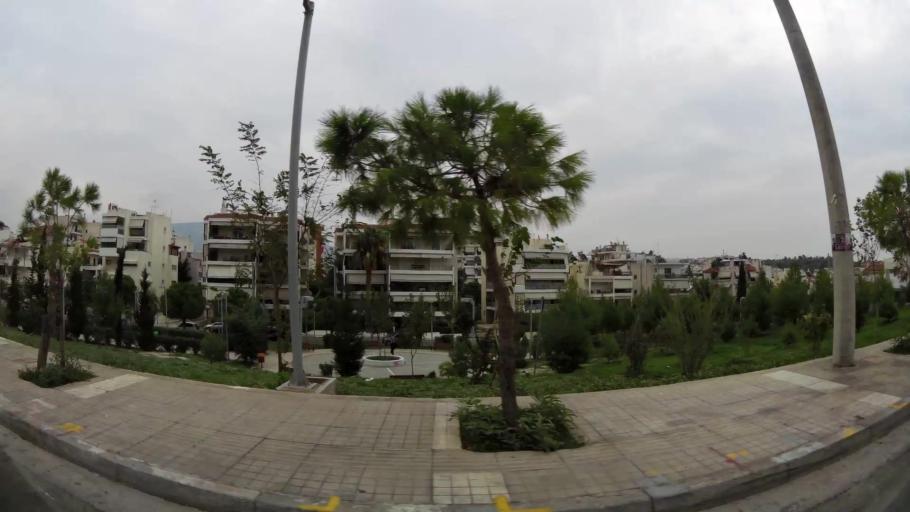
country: GR
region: Attica
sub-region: Nomarchia Athinas
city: Alimos
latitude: 37.9176
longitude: 23.7229
